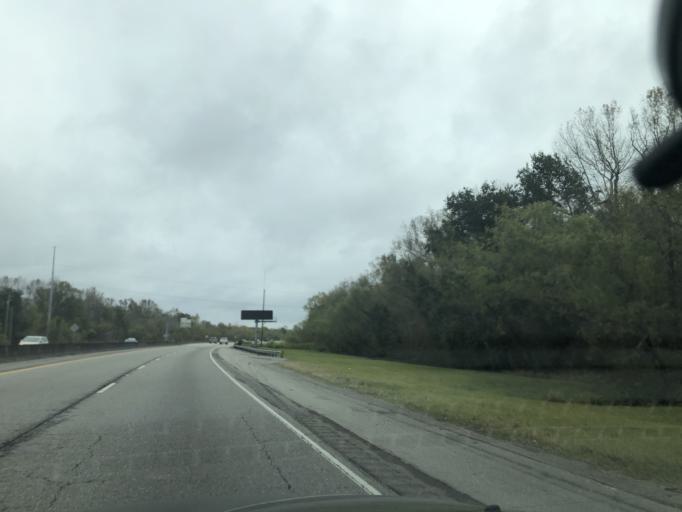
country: US
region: Louisiana
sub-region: Saint Charles Parish
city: Destrehan
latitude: 29.9582
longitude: -90.3648
